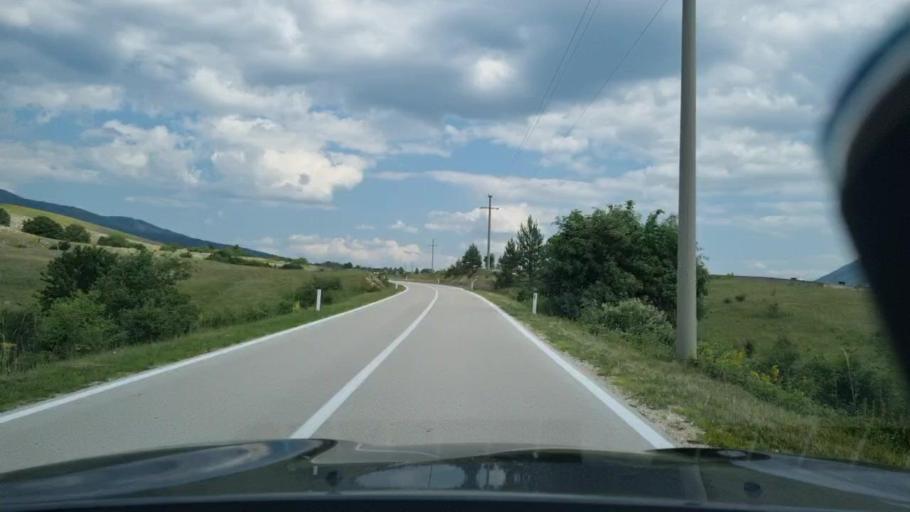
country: BA
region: Federation of Bosnia and Herzegovina
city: Bosansko Grahovo
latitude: 44.1276
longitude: 16.5164
